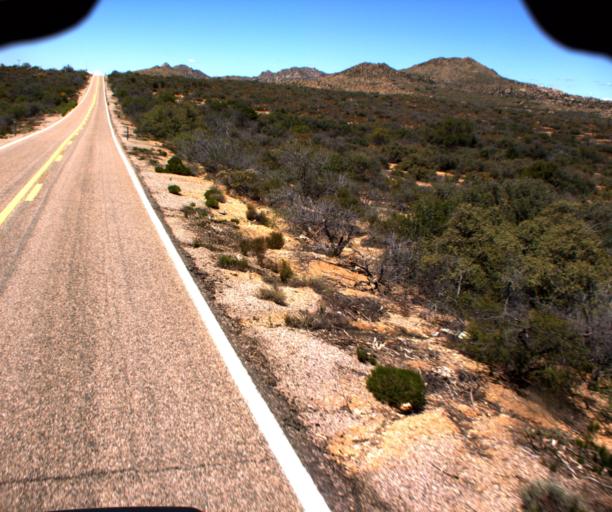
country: US
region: Arizona
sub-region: Yavapai County
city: Congress
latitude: 34.4345
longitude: -112.9245
